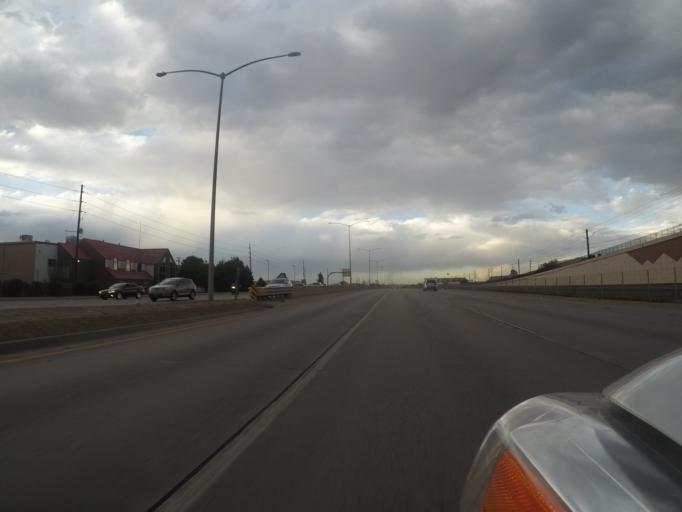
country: US
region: Colorado
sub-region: Arapahoe County
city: Littleton
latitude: 39.6327
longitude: -105.0084
